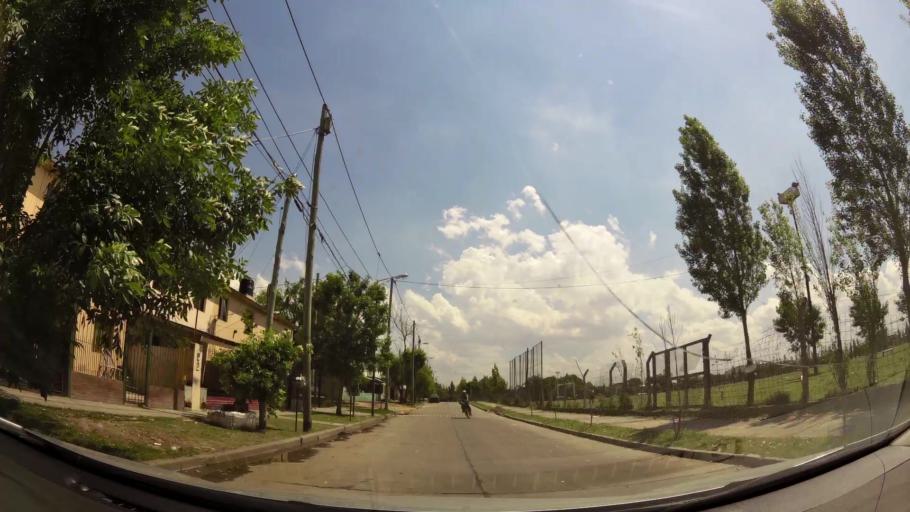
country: AR
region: Buenos Aires
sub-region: Partido de Tigre
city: Tigre
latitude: -34.4571
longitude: -58.5814
